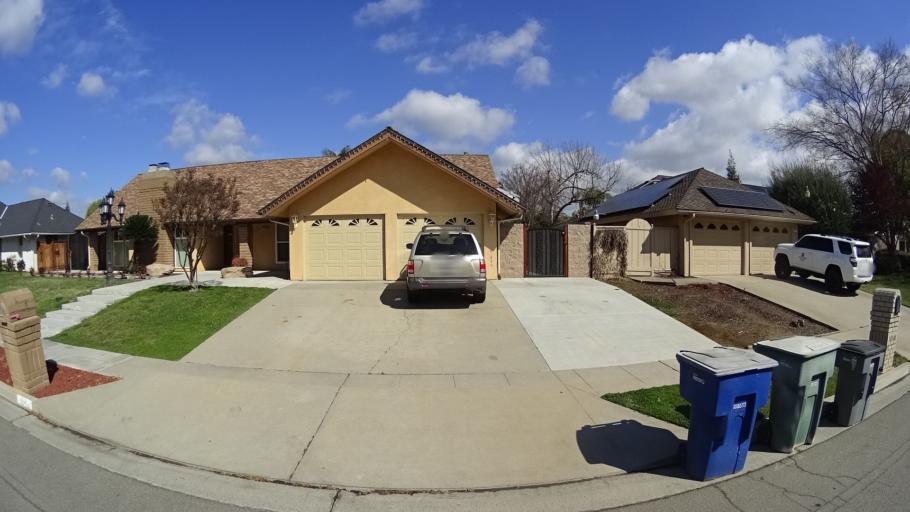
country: US
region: California
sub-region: Fresno County
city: Fresno
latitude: 36.8291
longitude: -119.8500
